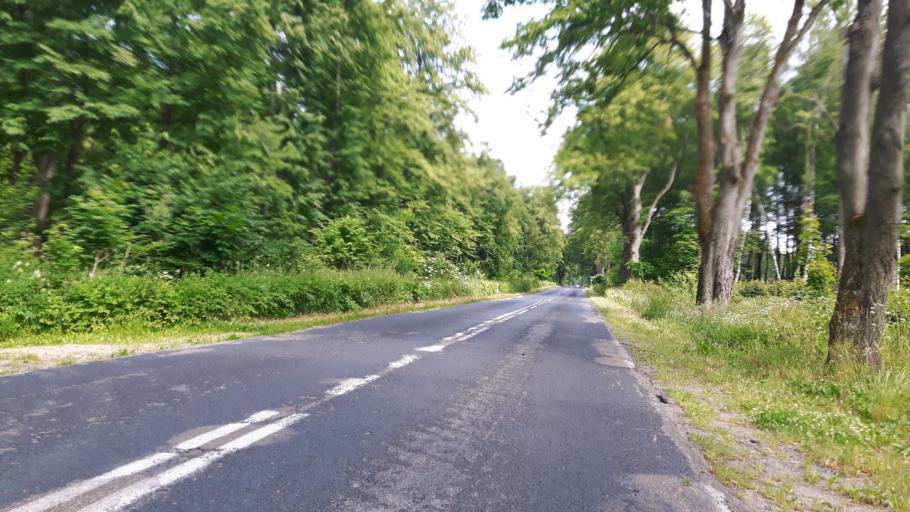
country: PL
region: Warmian-Masurian Voivodeship
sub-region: Powiat braniewski
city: Frombork
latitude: 54.3618
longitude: 19.7380
